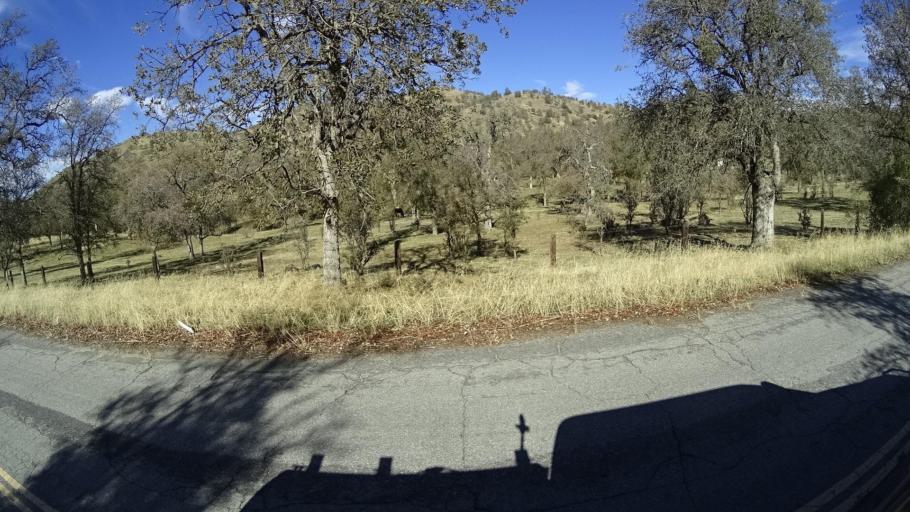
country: US
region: California
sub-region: Kern County
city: Alta Sierra
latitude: 35.6311
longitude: -118.7787
